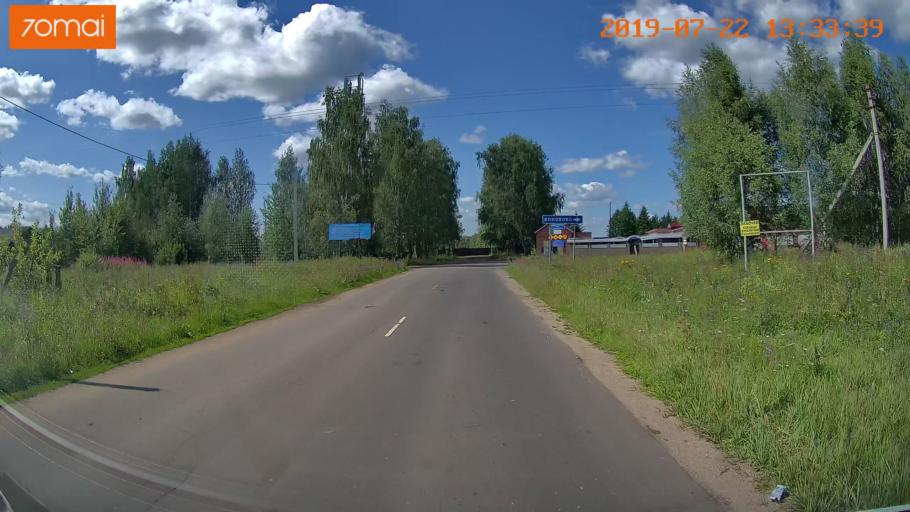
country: RU
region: Ivanovo
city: Novo-Talitsy
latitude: 57.0593
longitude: 40.8786
